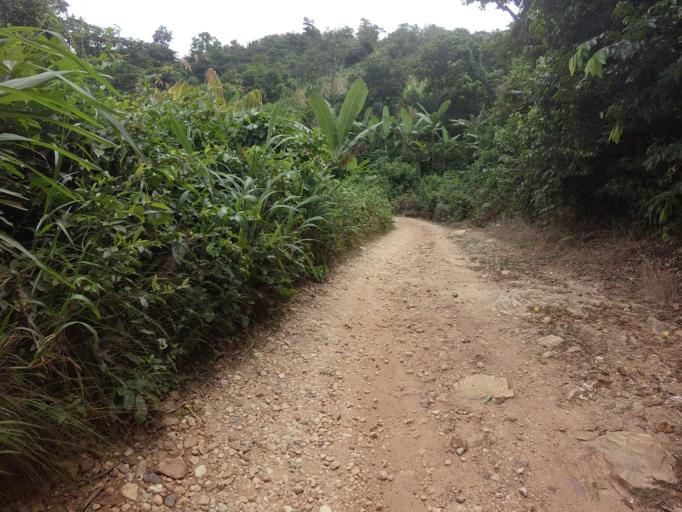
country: TG
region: Plateaux
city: Kpalime
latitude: 6.8652
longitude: 0.4404
